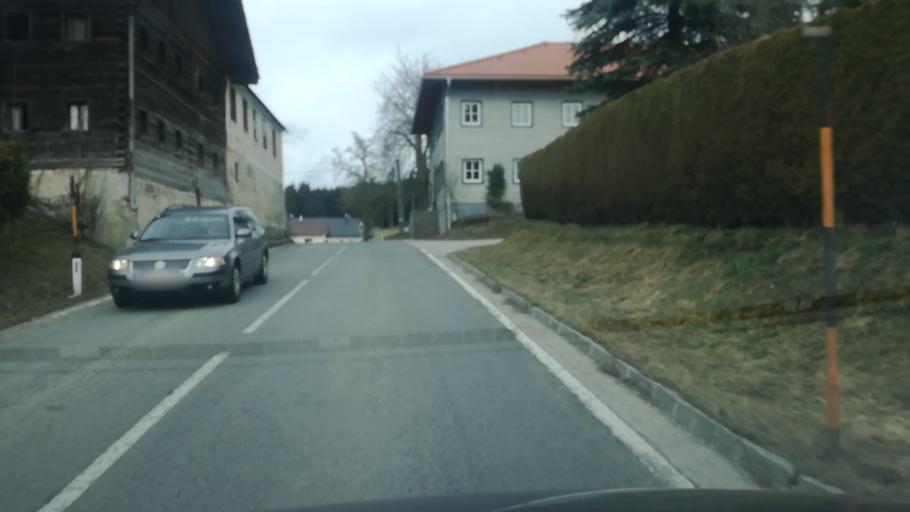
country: AT
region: Upper Austria
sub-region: Politischer Bezirk Vocklabruck
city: Frankenburg
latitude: 48.0960
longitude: 13.4866
